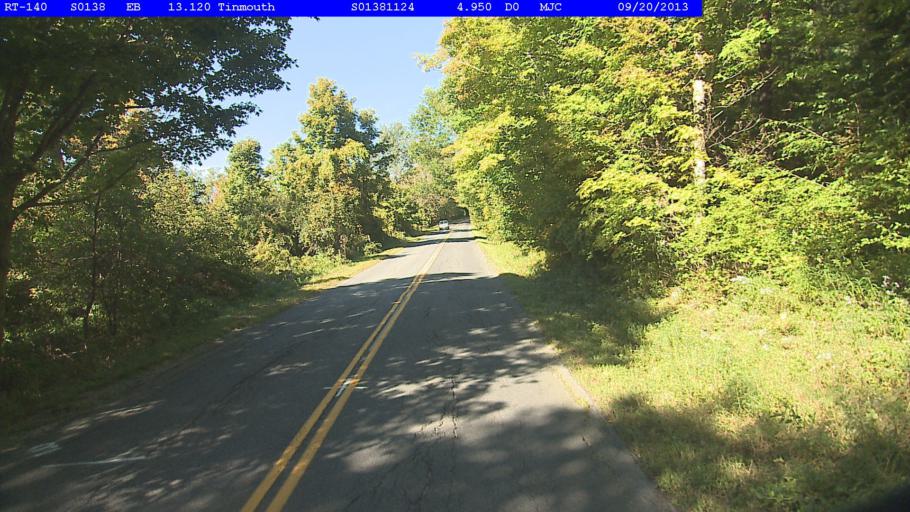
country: US
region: Vermont
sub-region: Rutland County
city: West Rutland
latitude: 43.4542
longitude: -73.0235
